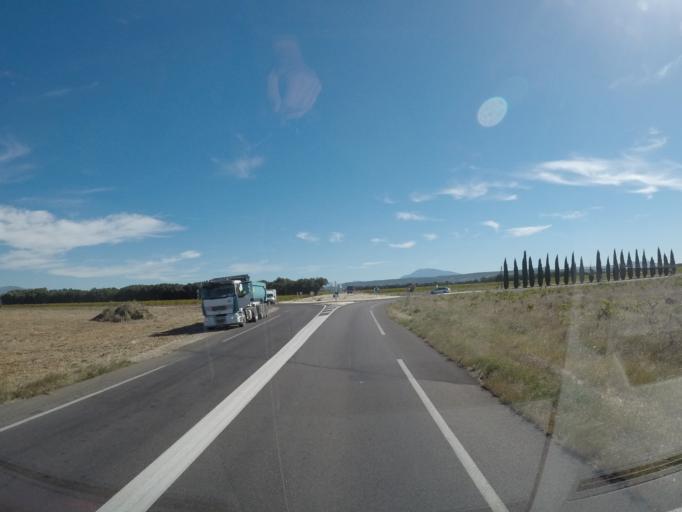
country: FR
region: Rhone-Alpes
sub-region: Departement de la Drome
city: Suze-la-Rousse
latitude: 44.2856
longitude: 4.8721
